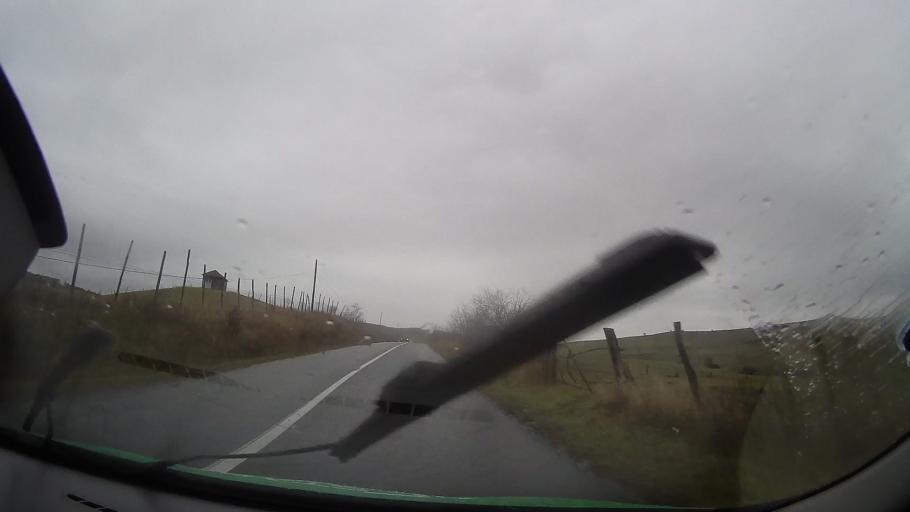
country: RO
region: Bistrita-Nasaud
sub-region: Comuna Monor
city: Monor
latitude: 46.9553
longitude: 24.6760
